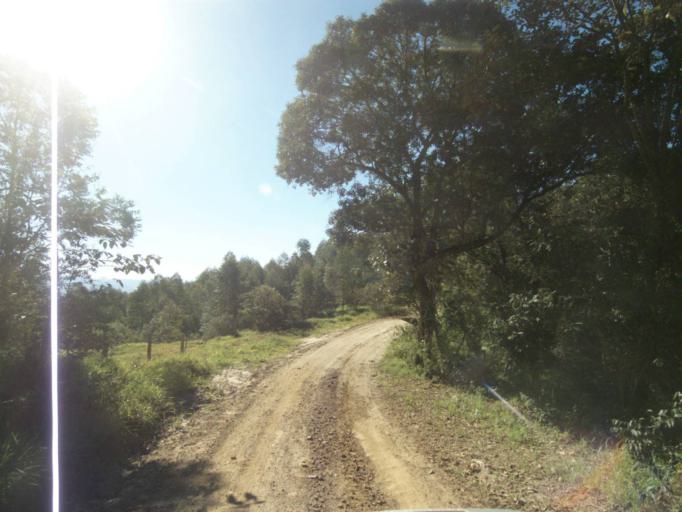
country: BR
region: Parana
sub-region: Tibagi
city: Tibagi
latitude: -24.5734
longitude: -50.4758
